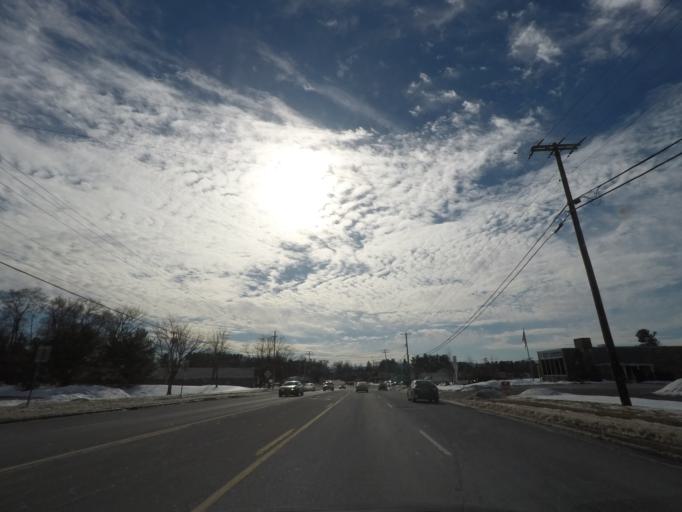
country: US
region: New York
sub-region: Albany County
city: Westmere
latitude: 42.6988
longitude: -73.8869
